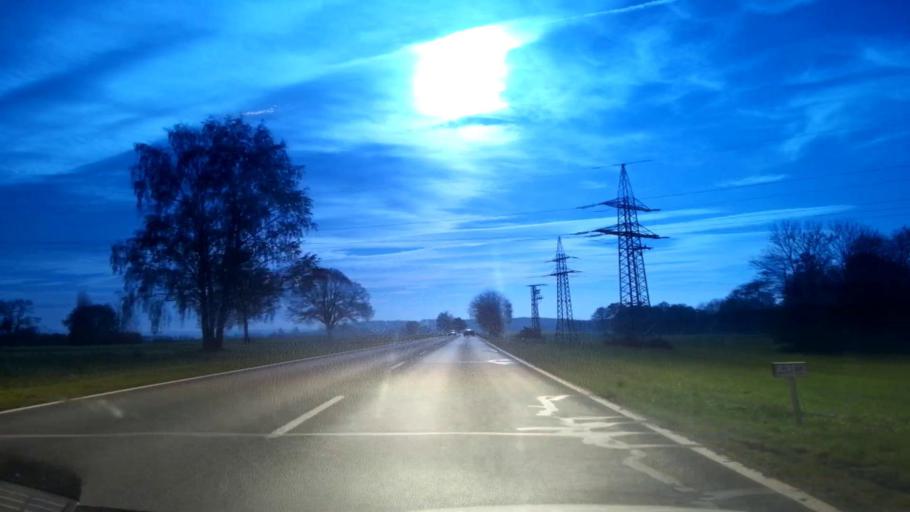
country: DE
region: Bavaria
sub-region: Upper Palatinate
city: Immenreuth
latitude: 49.9018
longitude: 11.8719
